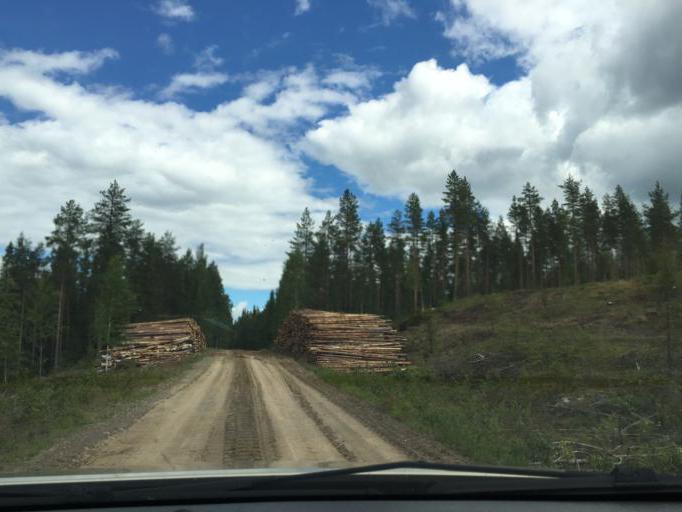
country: SE
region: Norrbotten
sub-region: Overkalix Kommun
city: OEverkalix
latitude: 66.1459
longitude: 22.7918
